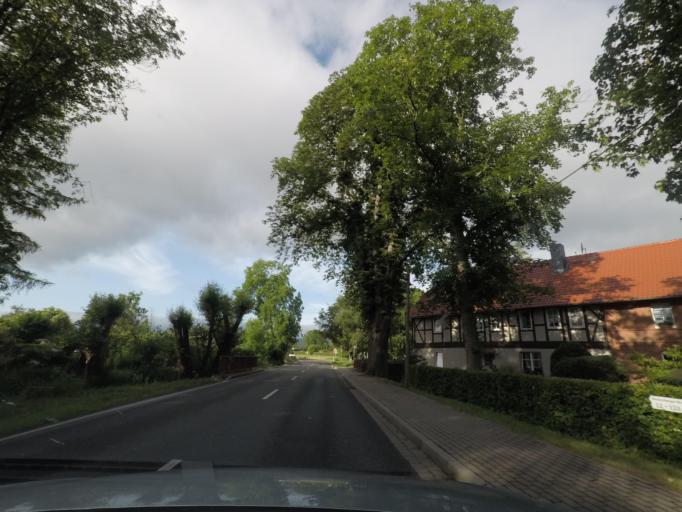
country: DE
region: Saxony-Anhalt
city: Derenburg
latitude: 51.8659
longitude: 10.9062
